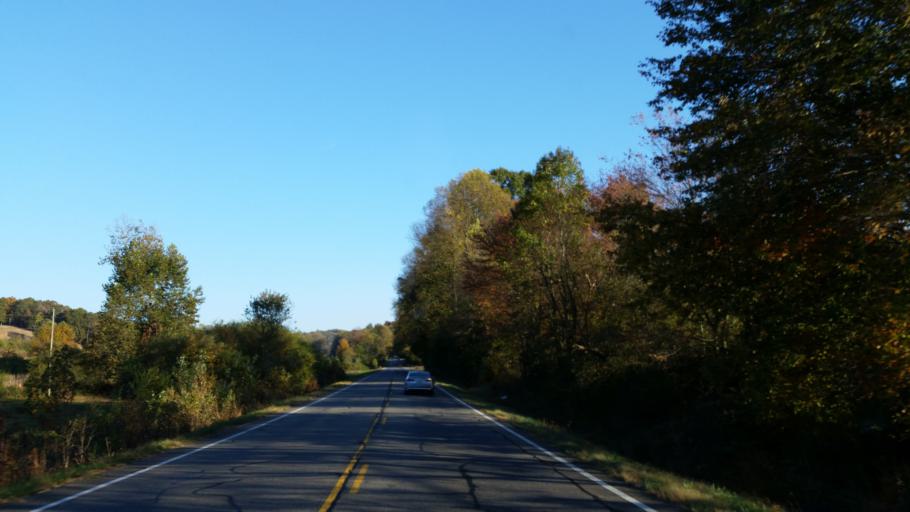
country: US
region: Georgia
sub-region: Gilmer County
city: Ellijay
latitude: 34.6069
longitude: -84.3523
